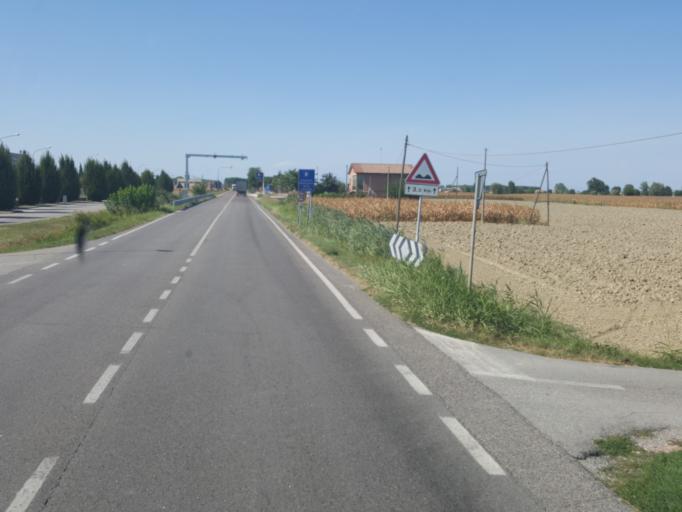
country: IT
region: Veneto
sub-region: Provincia di Rovigo
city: Ficarolo
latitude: 44.9587
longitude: 11.4430
